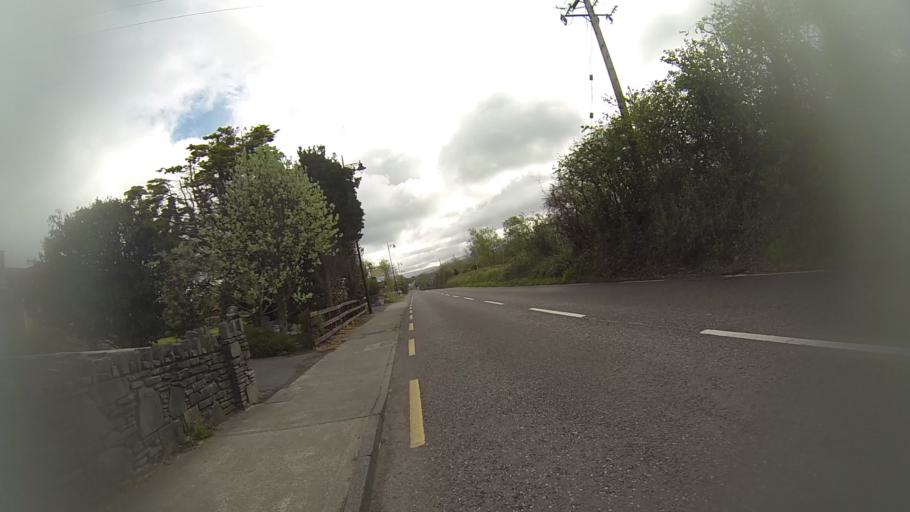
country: IE
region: Munster
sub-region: Ciarrai
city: Kenmare
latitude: 51.8825
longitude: -9.5978
